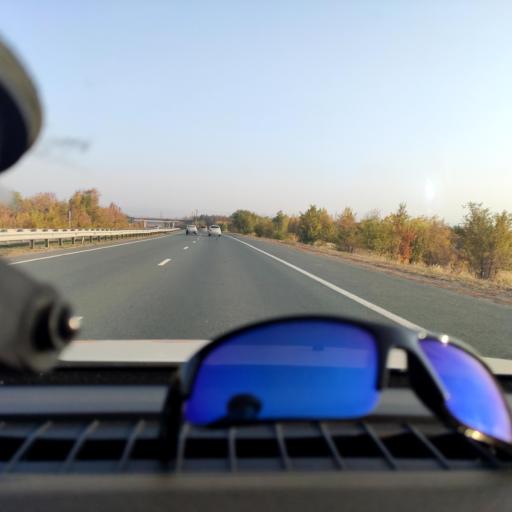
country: RU
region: Samara
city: Novokuybyshevsk
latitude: 53.0163
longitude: 49.9816
